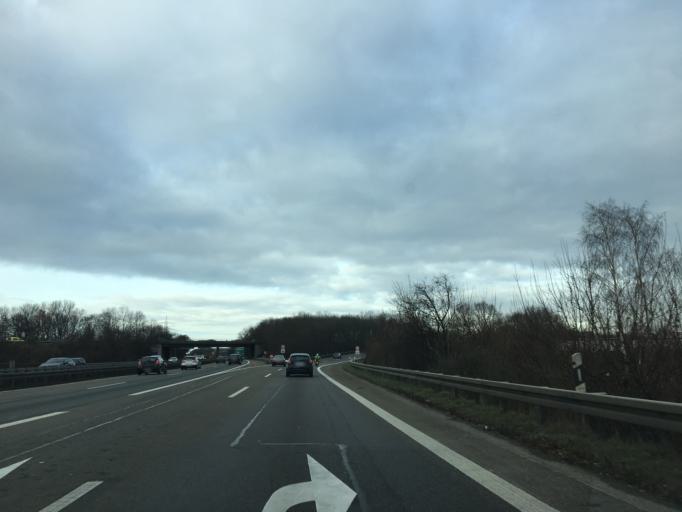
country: DE
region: North Rhine-Westphalia
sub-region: Regierungsbezirk Koln
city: Troisdorf
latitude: 50.7892
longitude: 7.1501
